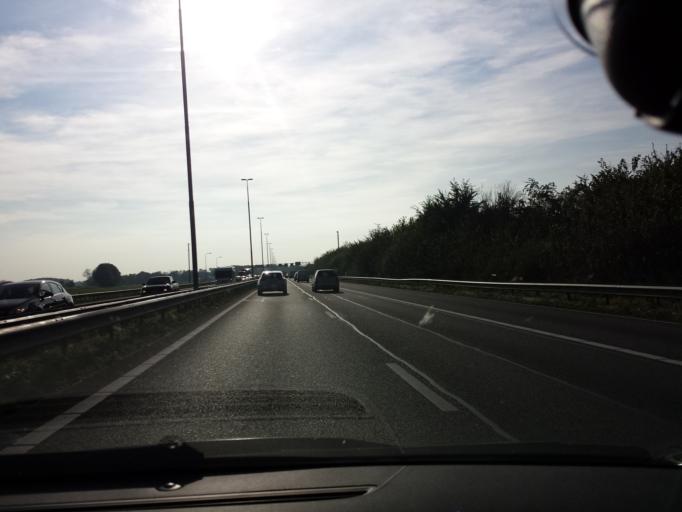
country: BE
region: Flanders
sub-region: Provincie Limburg
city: Maaseik
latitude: 51.0899
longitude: 5.8356
